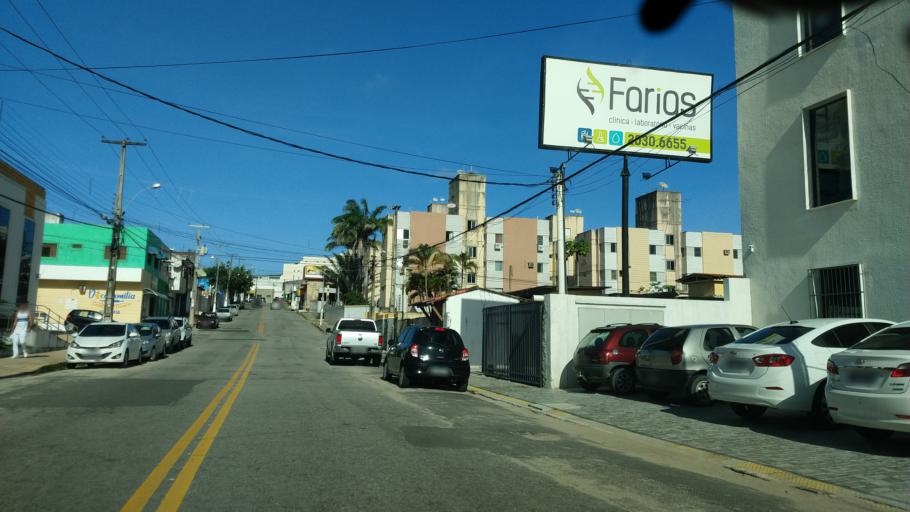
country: BR
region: Rio Grande do Norte
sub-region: Natal
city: Natal
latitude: -5.8253
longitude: -35.2050
